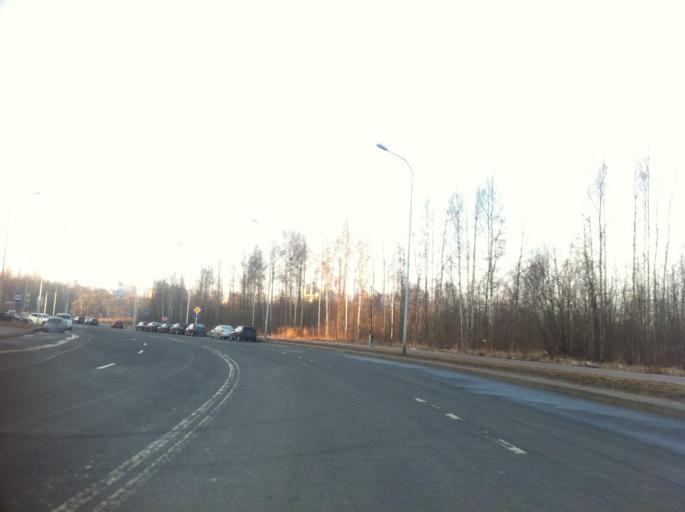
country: RU
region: St.-Petersburg
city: Sosnovaya Polyana
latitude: 59.8507
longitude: 30.1336
